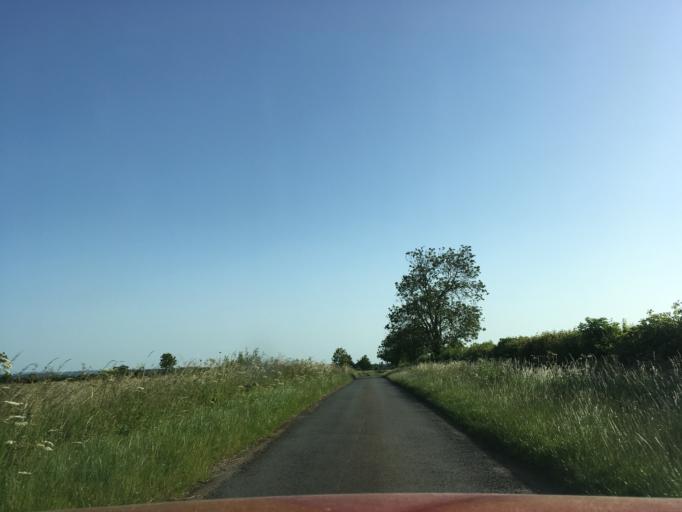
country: GB
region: England
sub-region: Gloucestershire
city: Fairford
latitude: 51.7217
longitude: -1.7619
